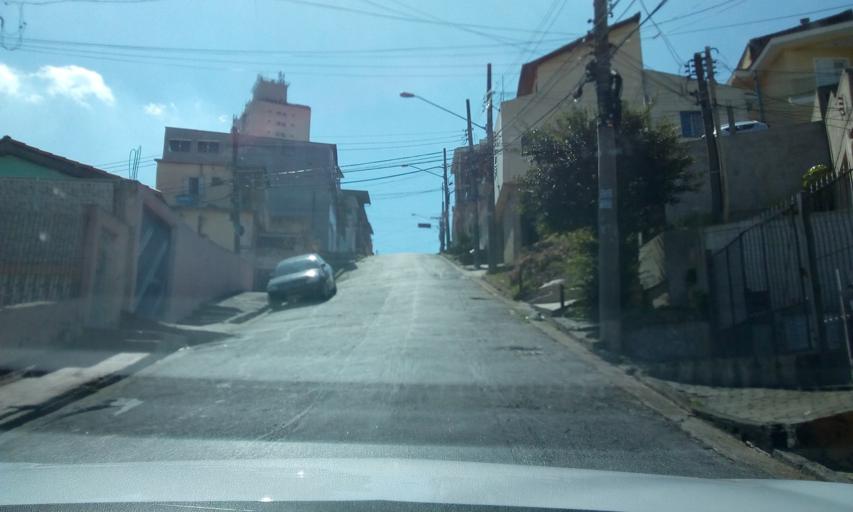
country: BR
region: Sao Paulo
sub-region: Guarulhos
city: Guarulhos
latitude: -23.4841
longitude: -46.5998
